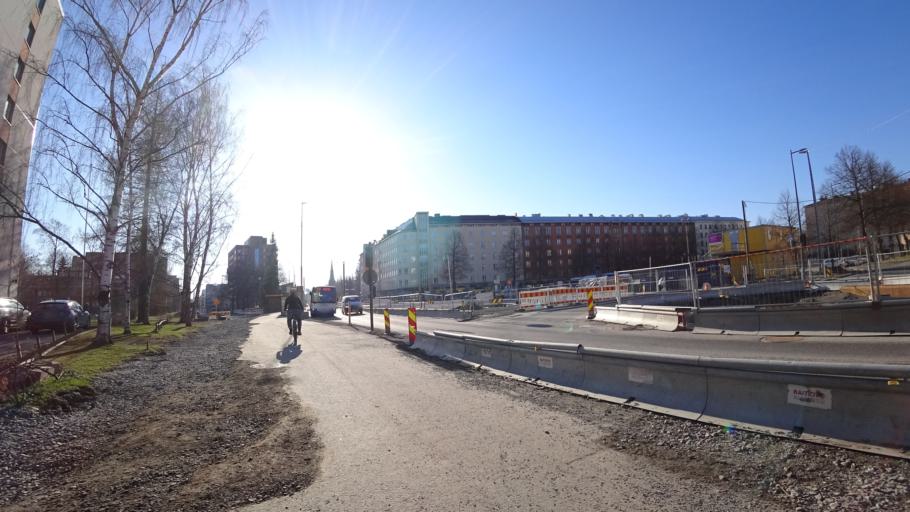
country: FI
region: Pirkanmaa
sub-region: Tampere
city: Tampere
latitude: 61.4981
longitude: 23.7410
